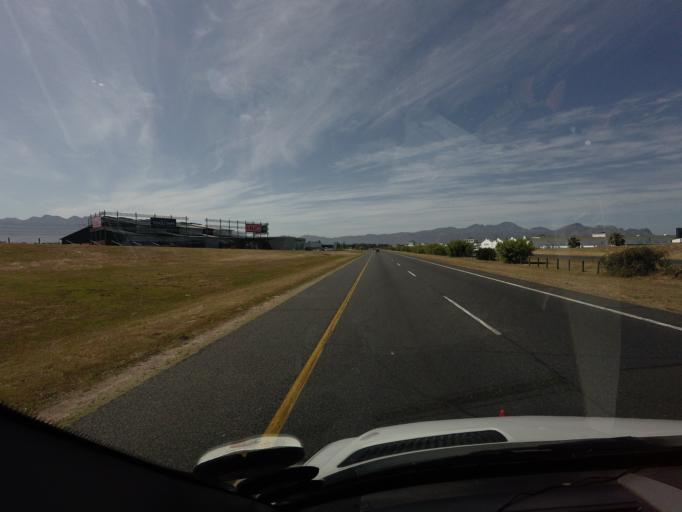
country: ZA
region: Western Cape
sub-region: Cape Winelands District Municipality
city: Stellenbosch
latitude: -34.0773
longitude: 18.8215
